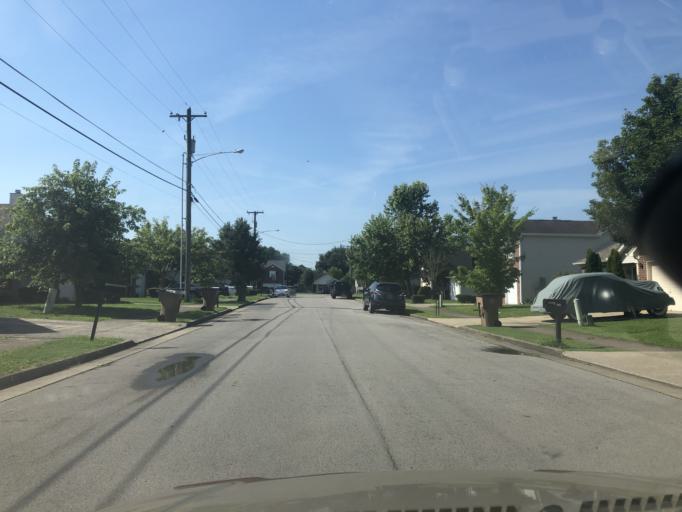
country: US
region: Tennessee
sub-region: Davidson County
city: Lakewood
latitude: 36.2403
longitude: -86.7019
